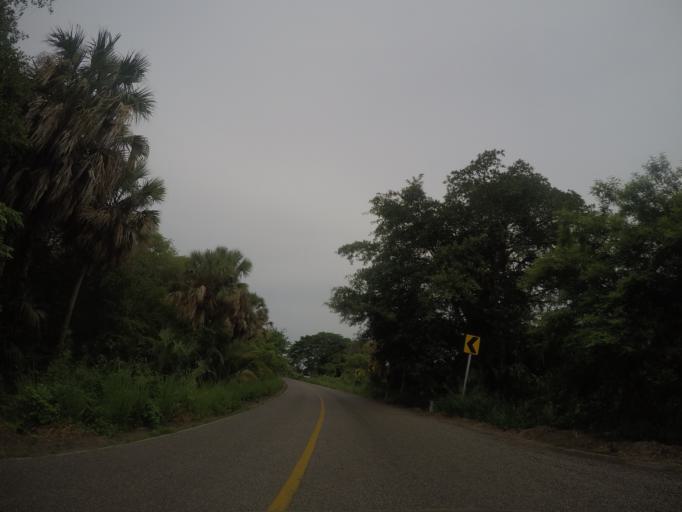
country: MX
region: Oaxaca
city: San Pedro Mixtepec
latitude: 15.9459
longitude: -97.1794
